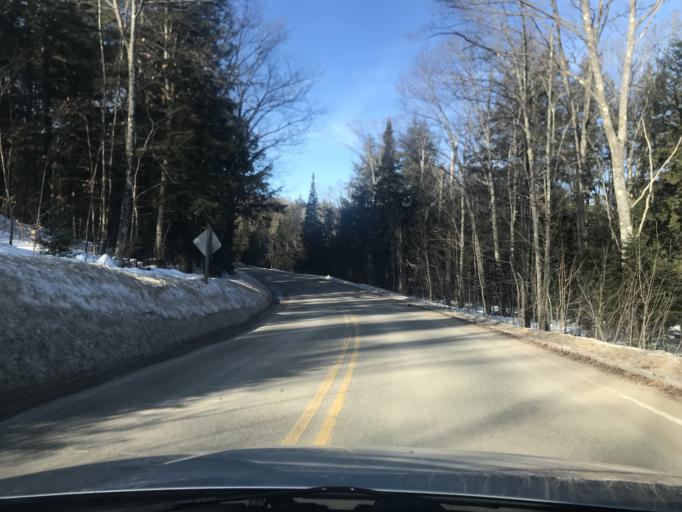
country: US
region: Michigan
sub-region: Dickinson County
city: Kingsford
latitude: 45.4104
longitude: -88.3538
